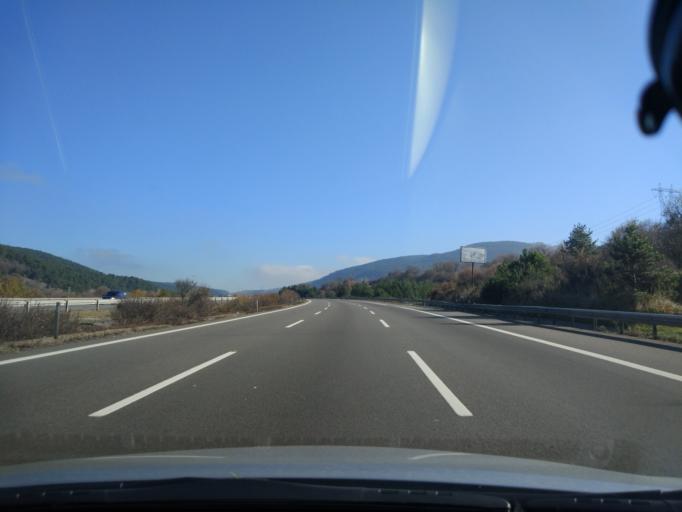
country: TR
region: Bolu
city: Gokcesu
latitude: 40.7392
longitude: 31.8327
